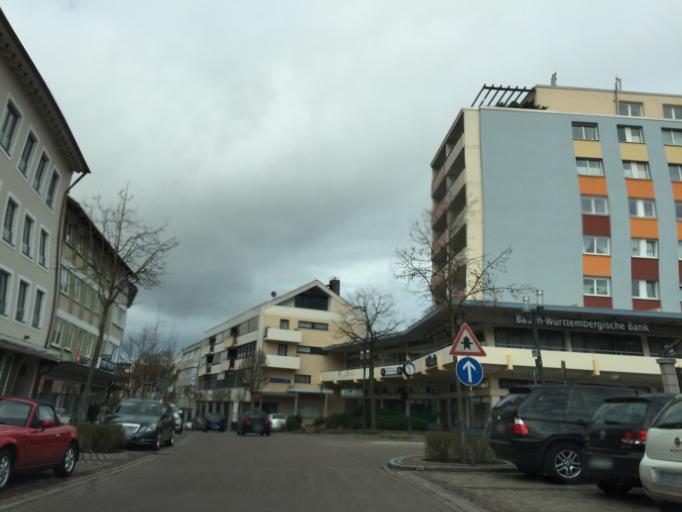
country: DE
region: Baden-Wuerttemberg
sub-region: Freiburg Region
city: Donaueschingen
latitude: 47.9529
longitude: 8.4994
